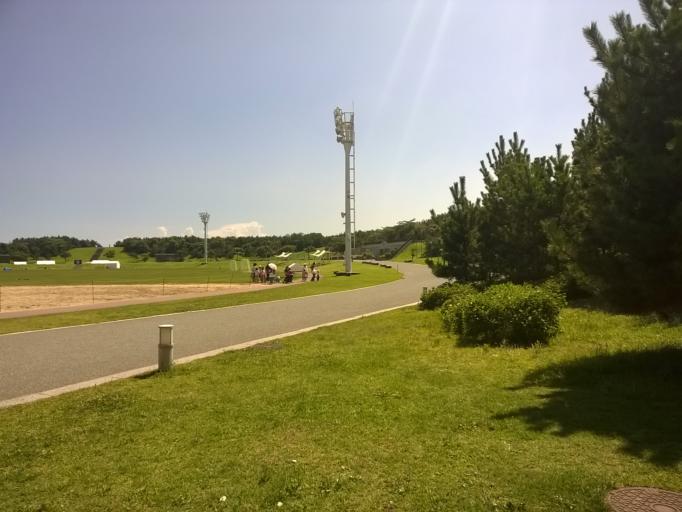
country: JP
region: Yamaguchi
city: Ogori-shimogo
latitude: 34.0041
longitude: 131.3706
